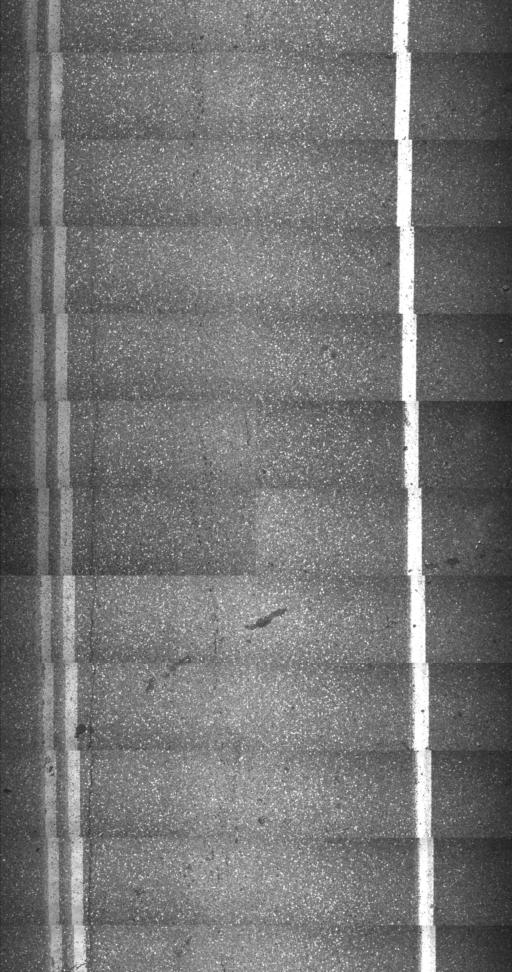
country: US
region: Vermont
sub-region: Orange County
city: Randolph
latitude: 44.0405
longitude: -72.7475
